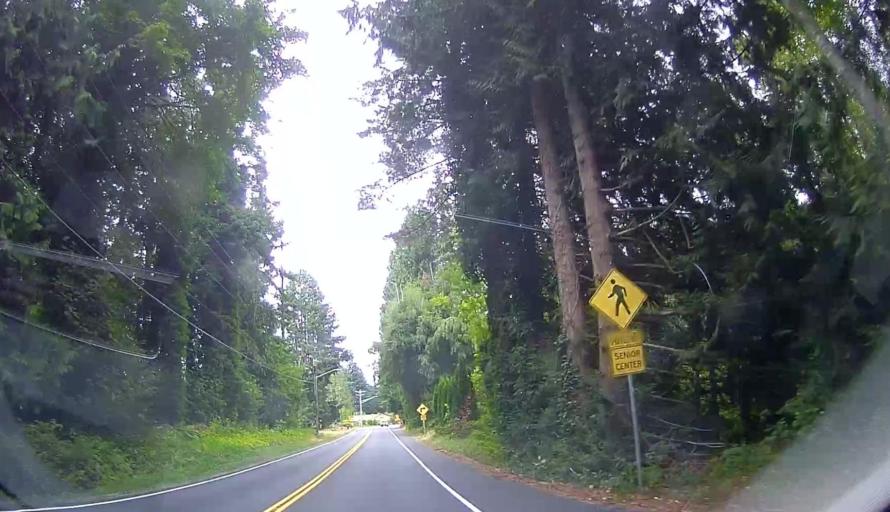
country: US
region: Washington
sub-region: Snohomish County
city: Warm Beach
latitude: 48.1800
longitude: -122.3519
